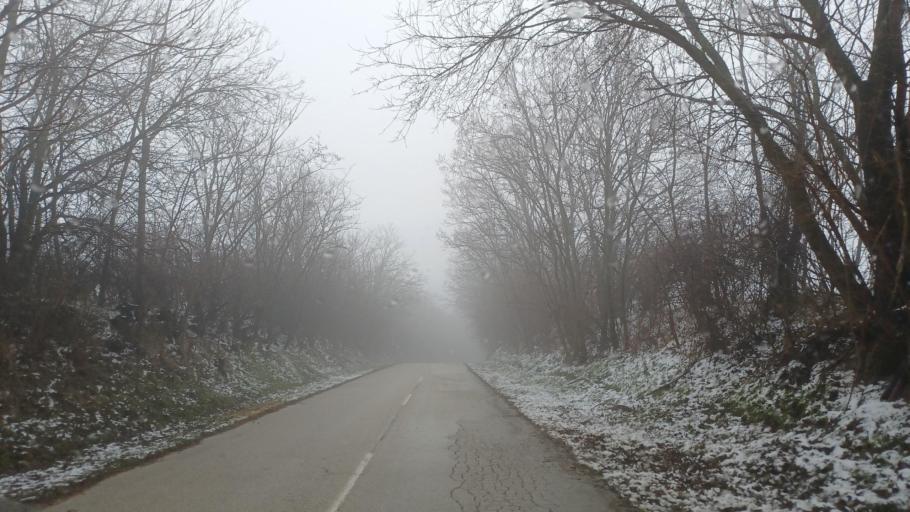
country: HU
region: Tolna
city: Gyonk
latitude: 46.6147
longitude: 18.4814
